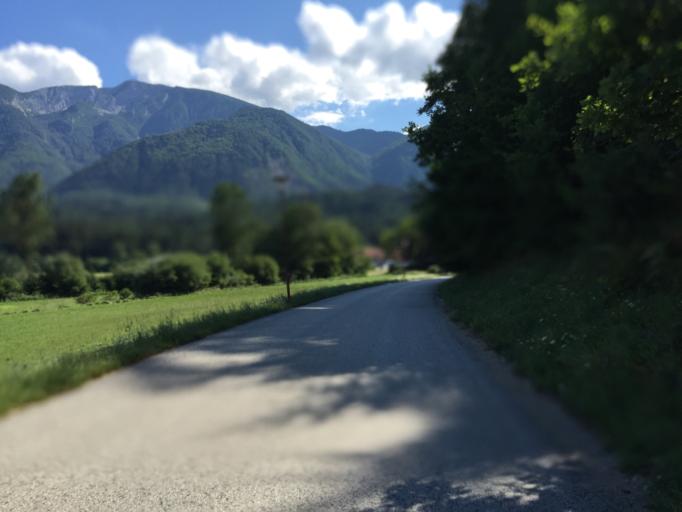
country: AT
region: Carinthia
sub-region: Politischer Bezirk Volkermarkt
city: Feistritz ob Bleiburg
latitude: 46.5603
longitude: 14.7536
